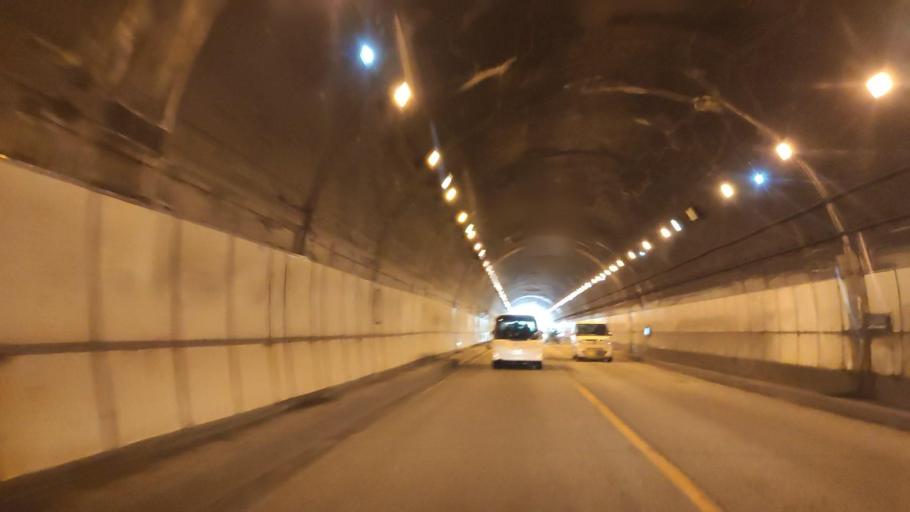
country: JP
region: Aomori
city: Aomori Shi
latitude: 40.8593
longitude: 140.8427
